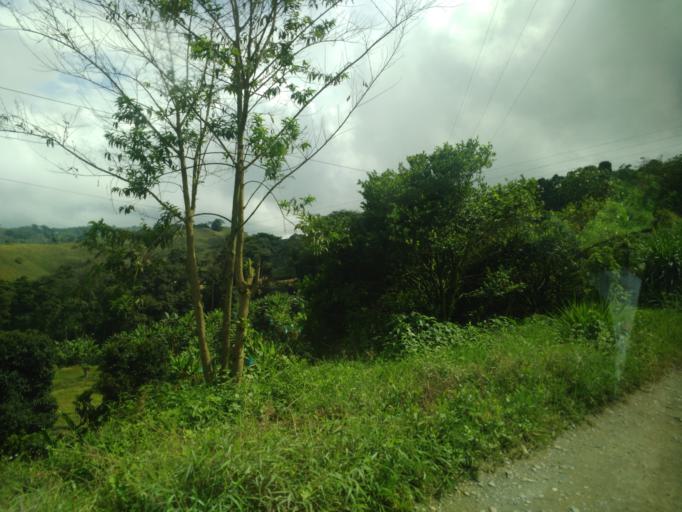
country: CO
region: Valle del Cauca
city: Sevilla
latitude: 4.2873
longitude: -75.9018
